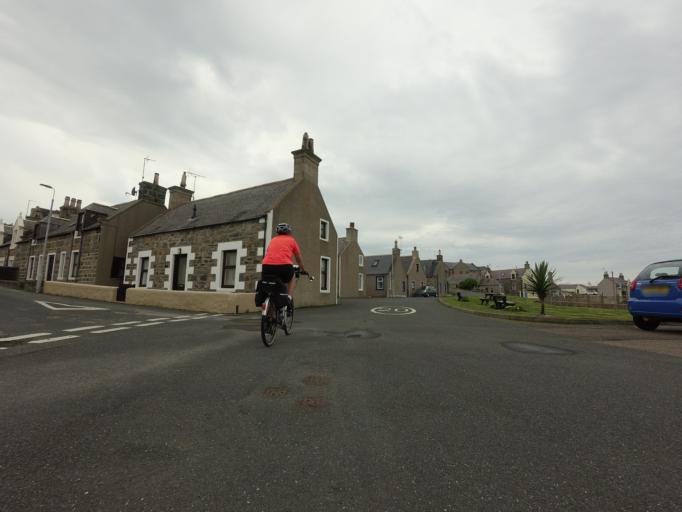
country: GB
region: Scotland
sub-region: Aberdeenshire
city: Whitehills
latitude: 57.6773
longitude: -2.5848
